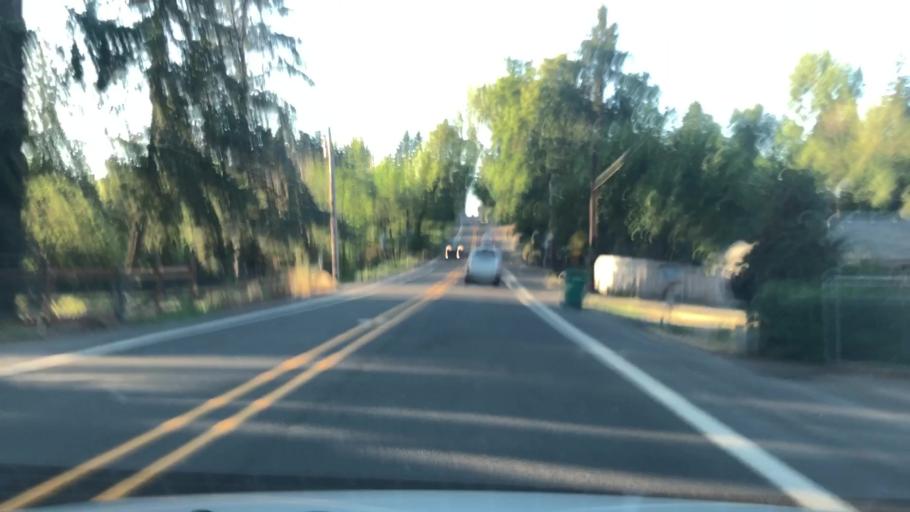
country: US
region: Oregon
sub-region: Clackamas County
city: Oak Grove
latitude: 45.4115
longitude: -122.6455
